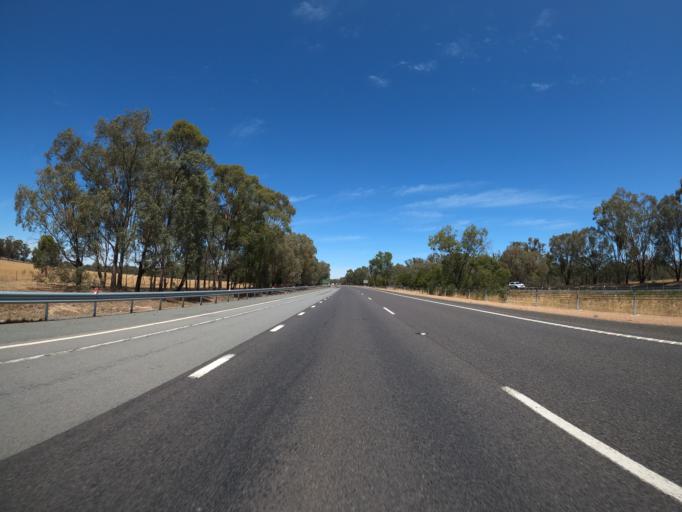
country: AU
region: Victoria
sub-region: Benalla
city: Benalla
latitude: -36.5778
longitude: 145.9171
